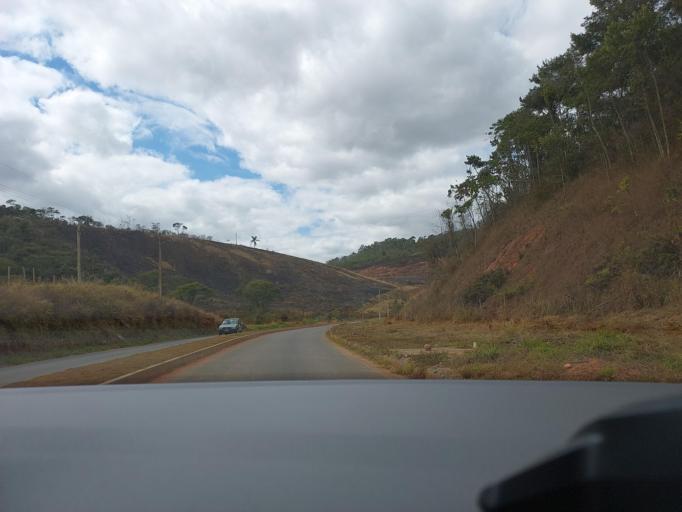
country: BR
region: Minas Gerais
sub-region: Vicosa
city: Vicosa
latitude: -20.7824
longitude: -42.8422
